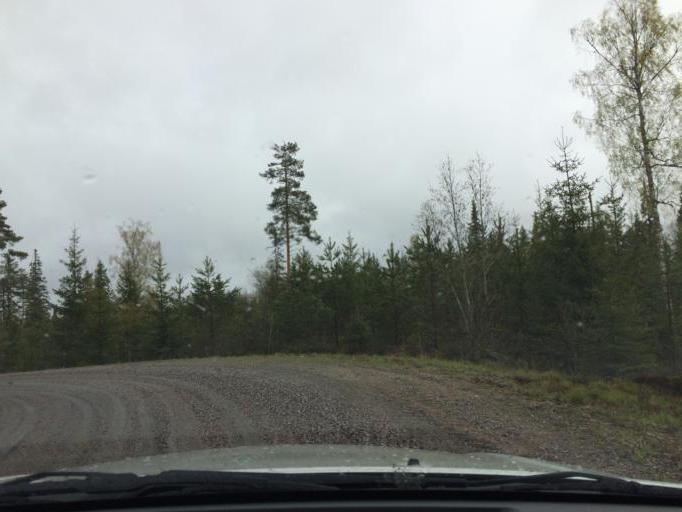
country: SE
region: OErebro
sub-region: Hallefors Kommun
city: Haellefors
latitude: 60.0144
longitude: 14.5930
